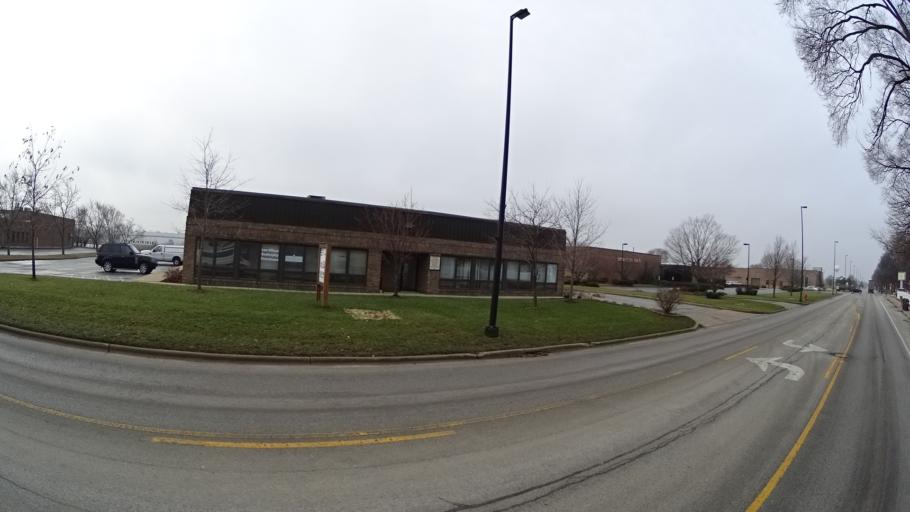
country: US
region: Illinois
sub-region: Cook County
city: East Hazel Crest
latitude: 41.5719
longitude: -87.6445
